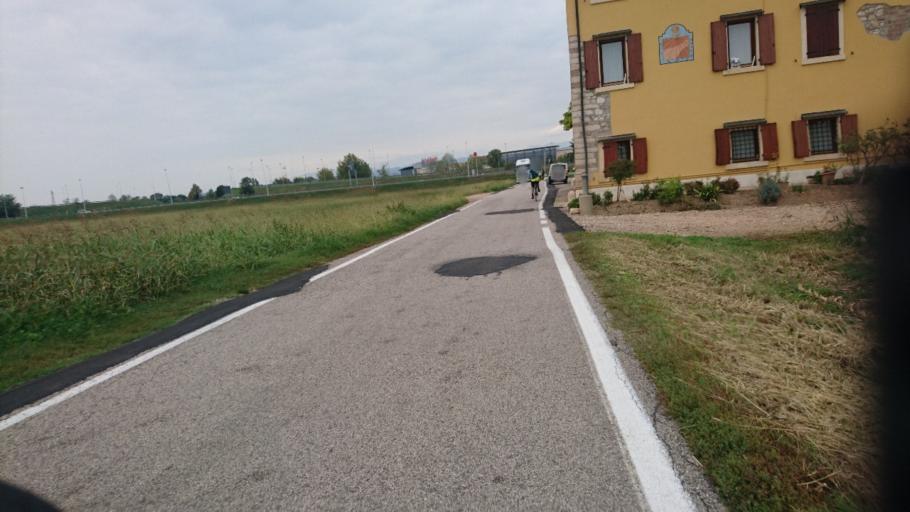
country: IT
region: Veneto
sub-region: Provincia di Verona
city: San Martino Buon Albergo
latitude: 45.4082
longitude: 11.0948
